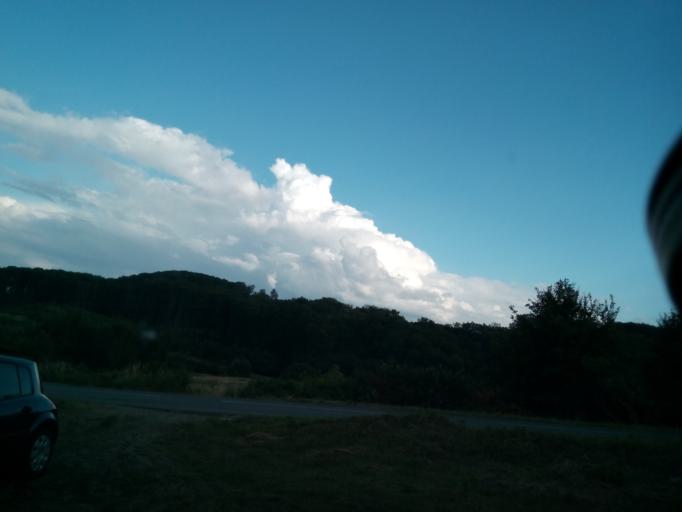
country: SK
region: Kosicky
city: Secovce
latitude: 48.6336
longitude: 21.4579
